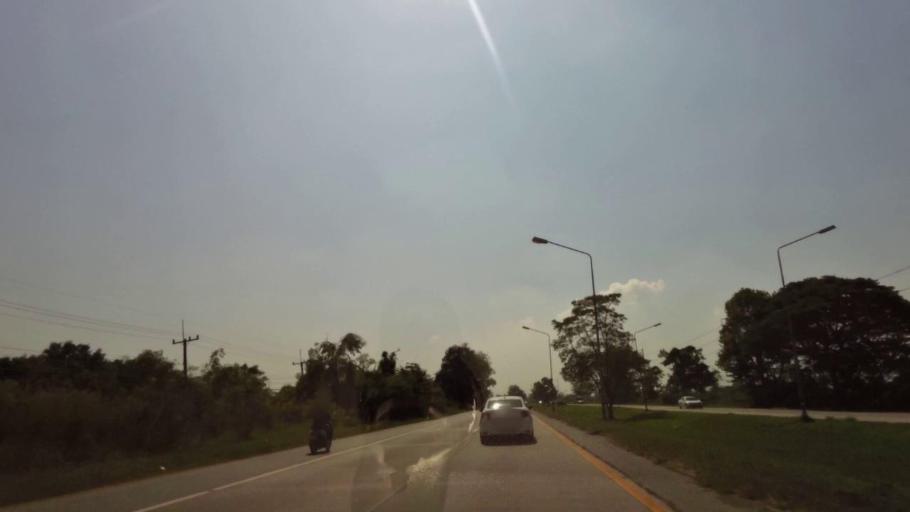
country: TH
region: Phichit
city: Wachira Barami
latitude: 16.5962
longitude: 100.1472
